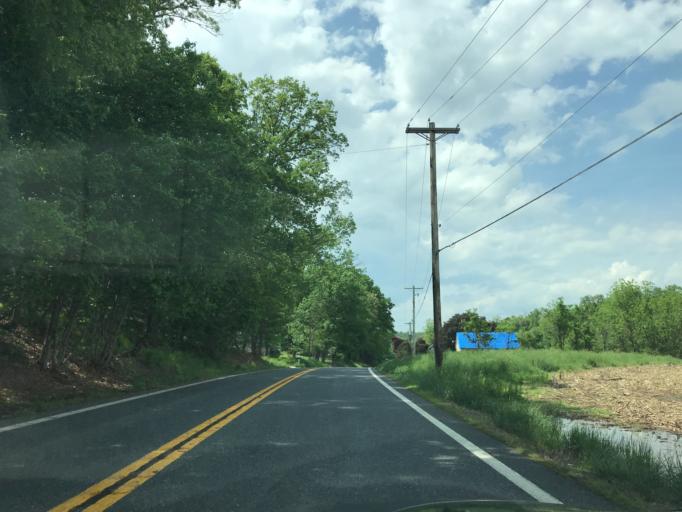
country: US
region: Pennsylvania
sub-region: York County
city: Susquehanna Trails
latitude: 39.6801
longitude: -76.3707
